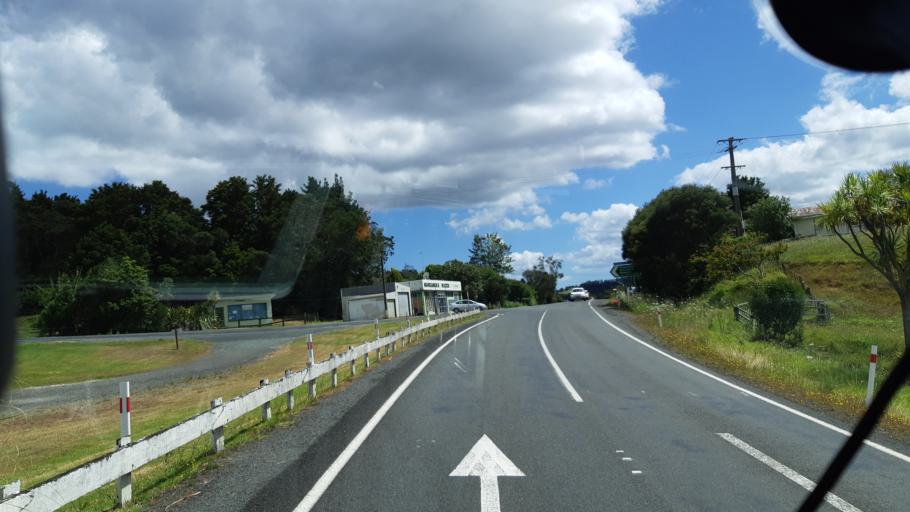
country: NZ
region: Northland
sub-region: Far North District
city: Taipa
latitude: -35.2379
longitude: 173.5439
